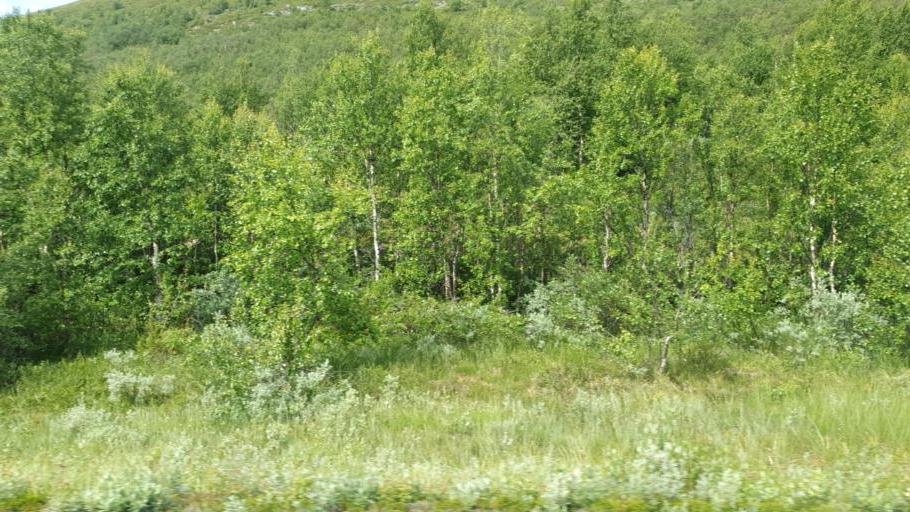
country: NO
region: Oppland
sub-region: Vaga
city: Vagamo
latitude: 61.5292
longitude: 8.8787
